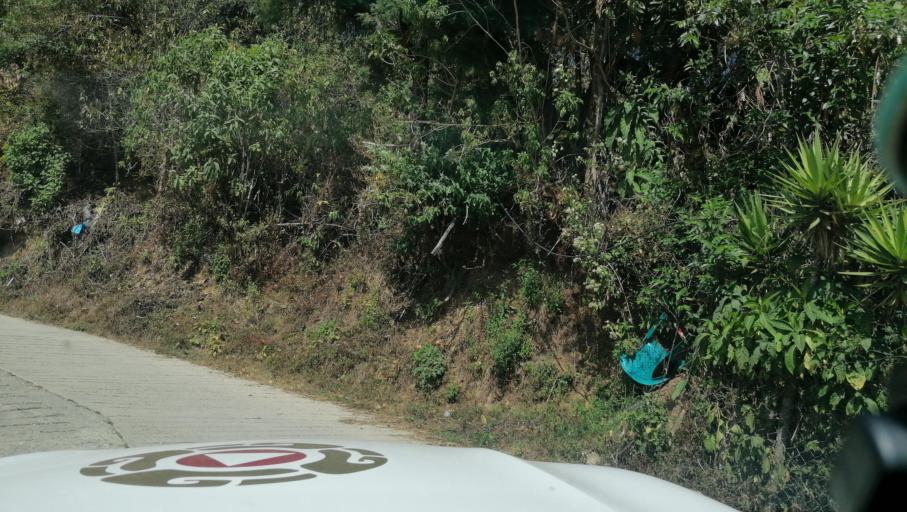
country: GT
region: San Marcos
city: Tacana
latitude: 15.2031
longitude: -92.1993
